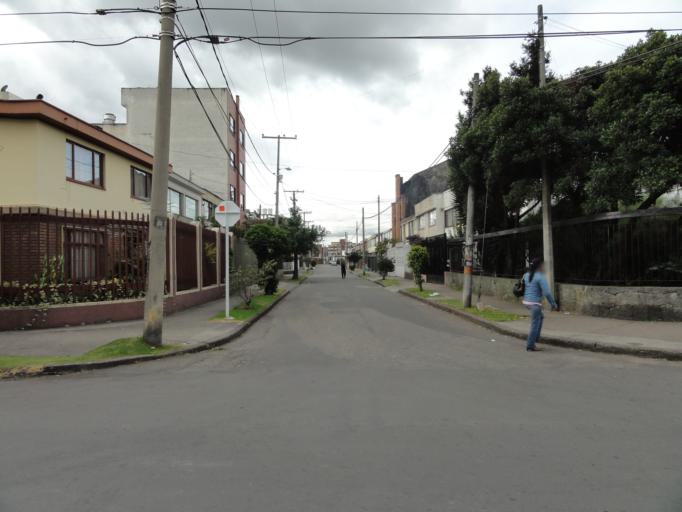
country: CO
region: Bogota D.C.
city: Bogota
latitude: 4.6475
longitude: -74.0802
